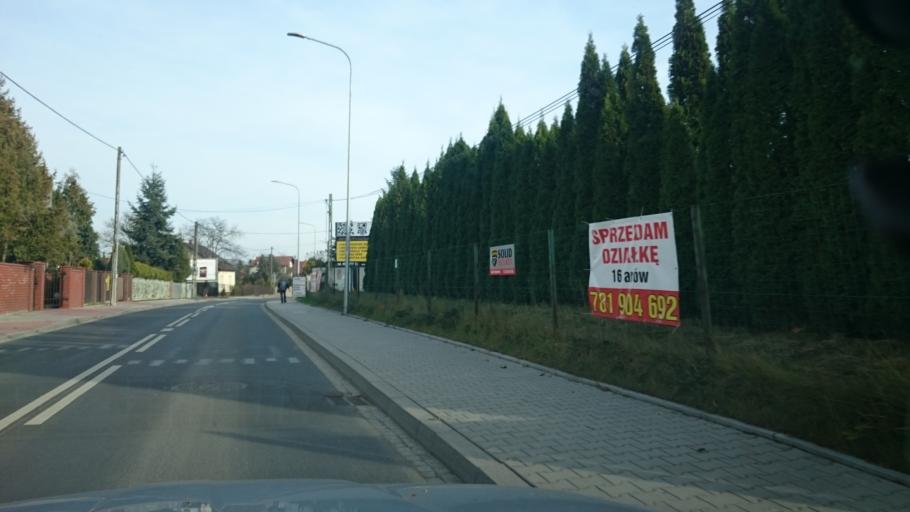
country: PL
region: Lesser Poland Voivodeship
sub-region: Powiat wielicki
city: Czarnochowice
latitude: 50.0215
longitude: 20.0102
